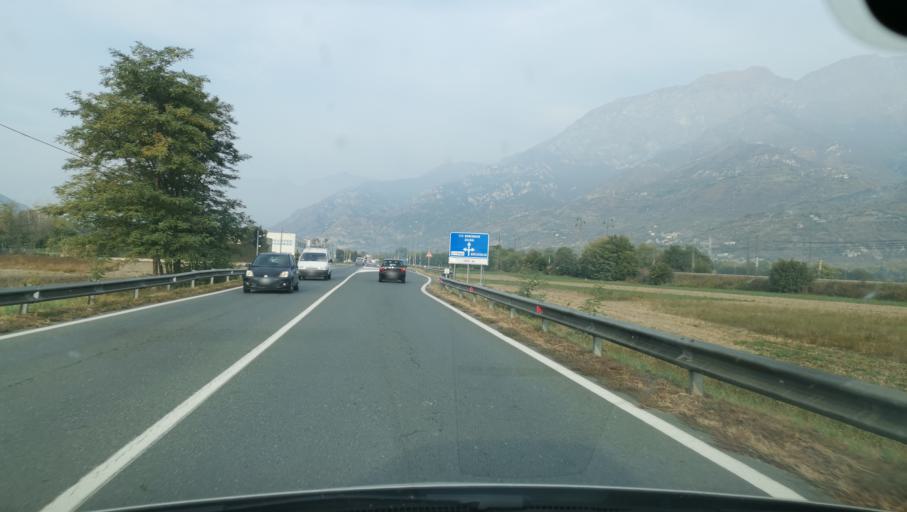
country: IT
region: Piedmont
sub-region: Provincia di Torino
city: Bruzolo
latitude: 45.1316
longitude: 7.1961
